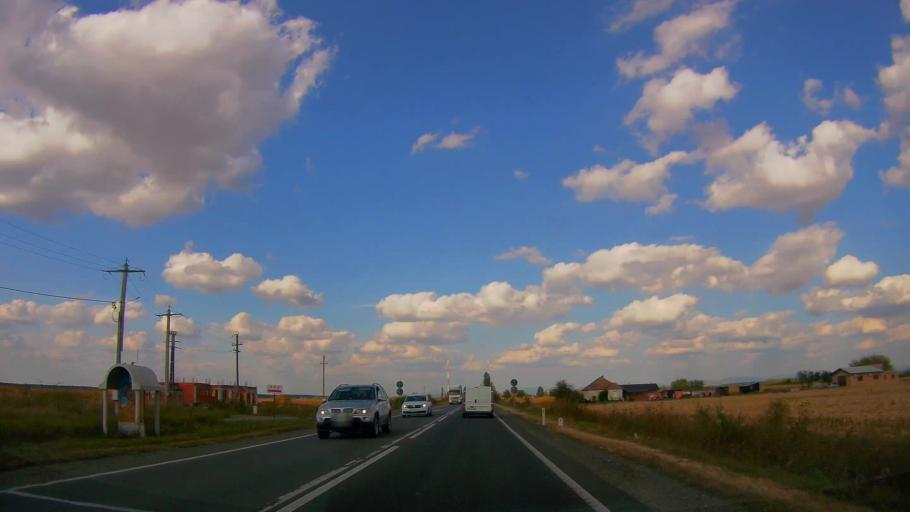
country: RO
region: Satu Mare
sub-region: Comuna Botiz
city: Botiz
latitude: 47.8422
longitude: 22.9632
